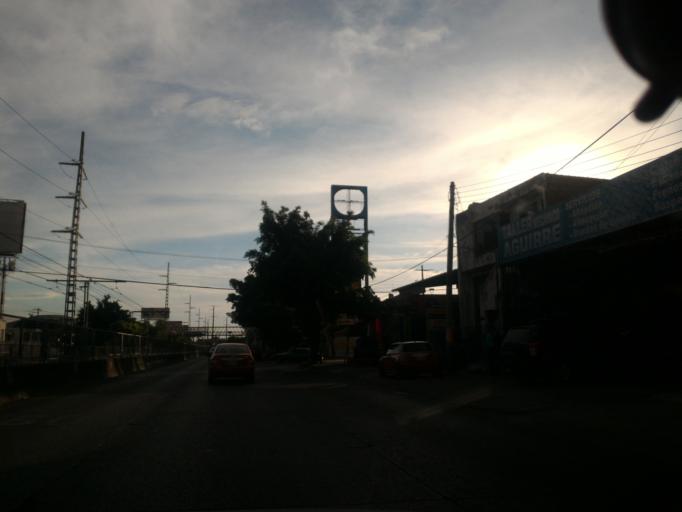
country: MX
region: Jalisco
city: Guadalajara
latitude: 20.6316
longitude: -103.3816
